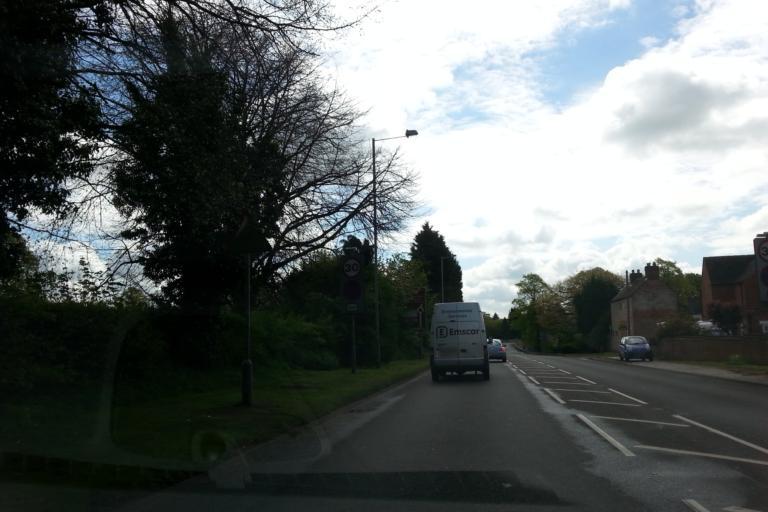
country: GB
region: England
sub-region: Staffordshire
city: Lichfield
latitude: 52.6812
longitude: -1.8378
